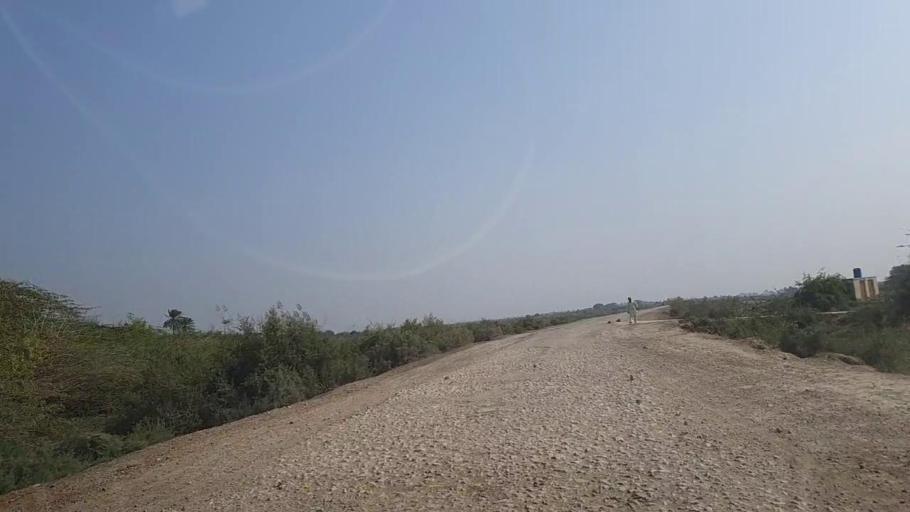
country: PK
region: Sindh
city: Keti Bandar
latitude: 24.2542
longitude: 67.6243
